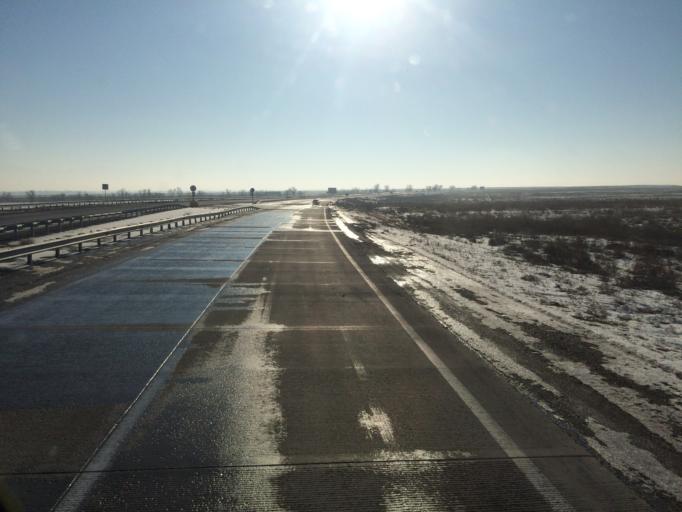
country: KG
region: Chuy
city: Kara-Balta
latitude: 43.1868
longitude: 73.9414
